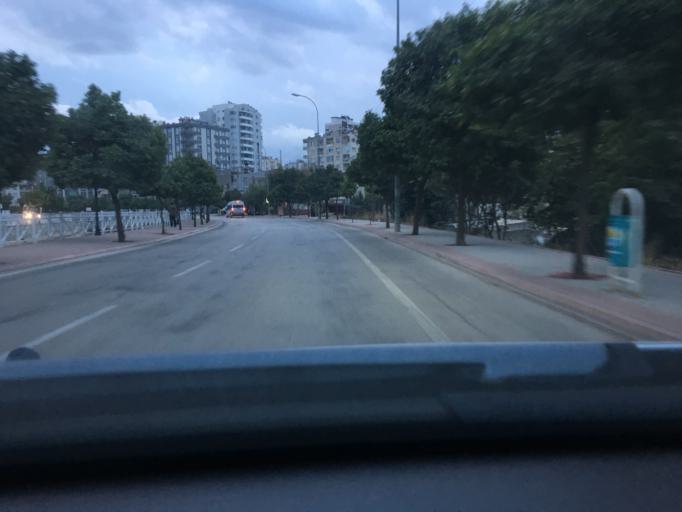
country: TR
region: Adana
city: Seyhan
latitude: 37.0290
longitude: 35.2826
